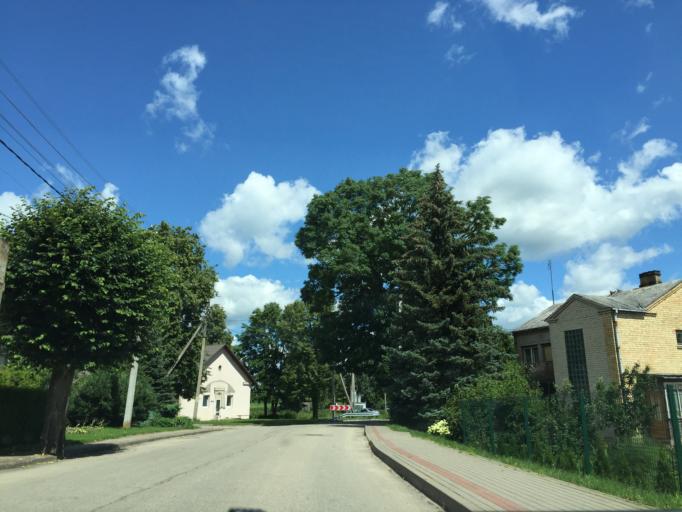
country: LT
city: Ramygala
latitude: 55.5144
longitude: 24.3043
